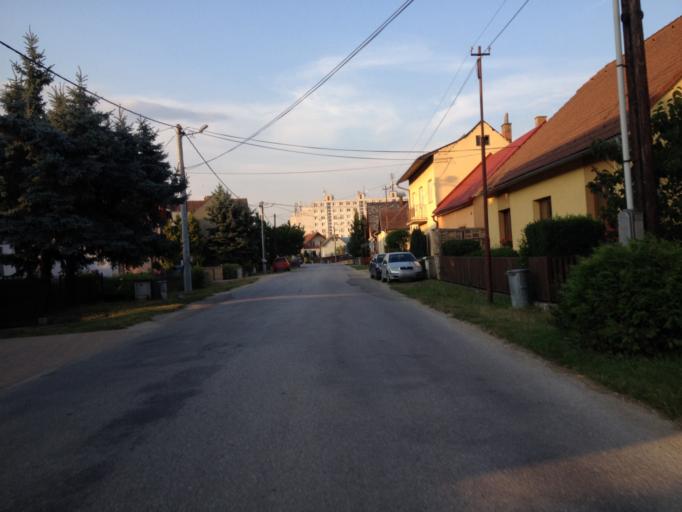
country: SK
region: Nitriansky
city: Puchov
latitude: 49.0587
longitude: 18.3203
